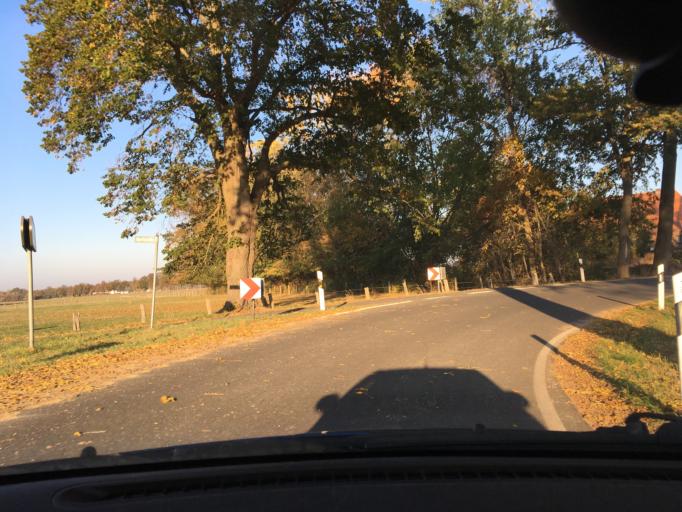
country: DE
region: Lower Saxony
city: Bleckede
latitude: 53.3201
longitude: 10.7947
